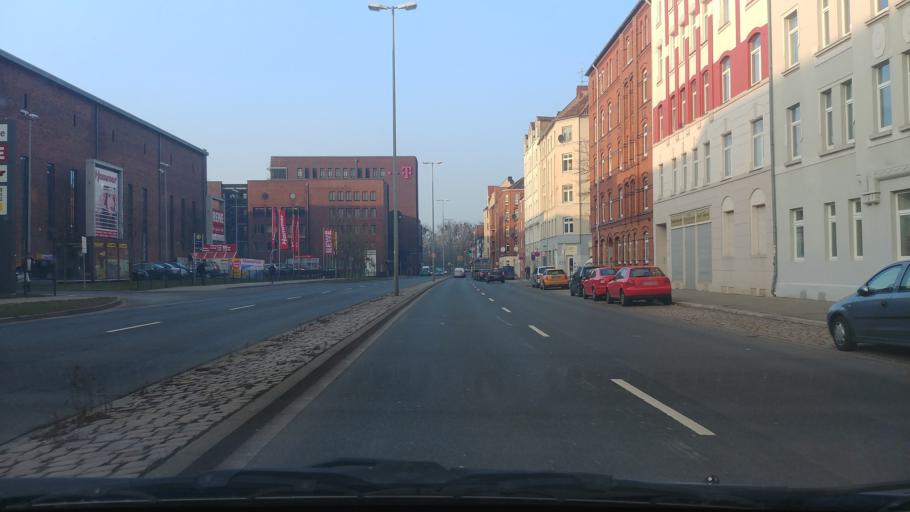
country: DE
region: Lower Saxony
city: Hannover
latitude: 52.3573
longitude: 9.7167
